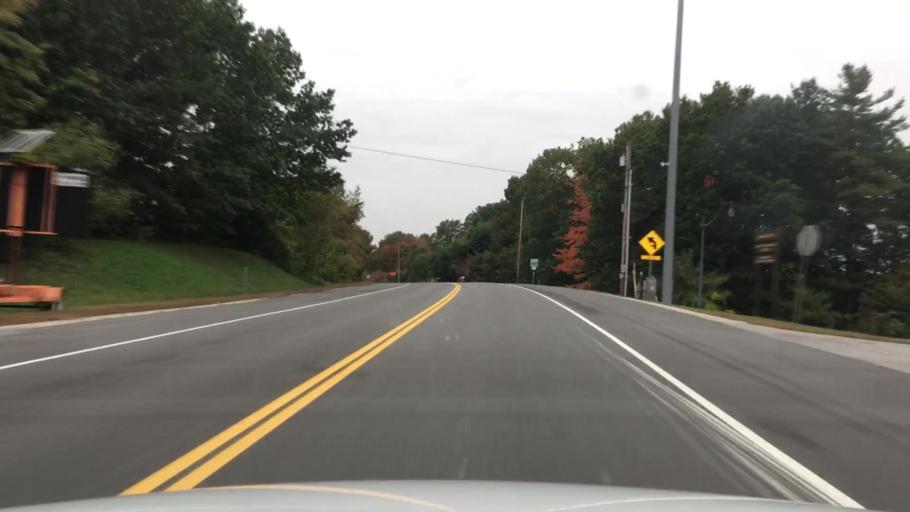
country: US
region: Maine
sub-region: York County
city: Eliot
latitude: 43.1301
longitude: -70.8528
